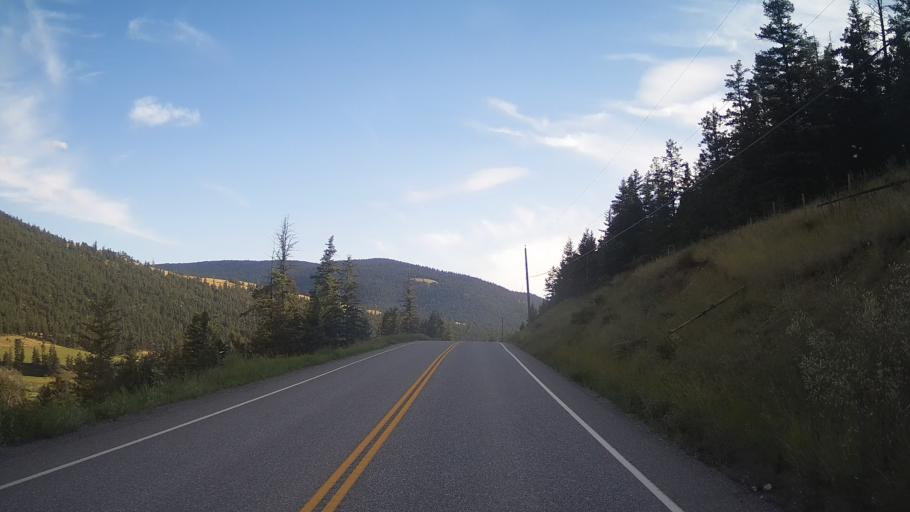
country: CA
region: British Columbia
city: Cache Creek
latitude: 50.8482
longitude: -121.5390
